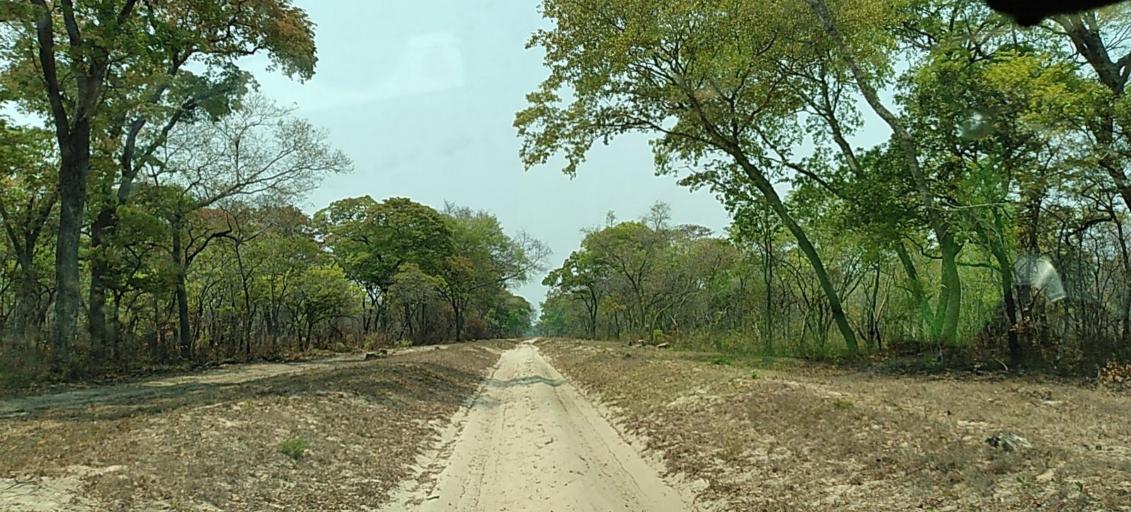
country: ZM
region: Western
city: Lukulu
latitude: -14.1365
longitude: 23.2766
